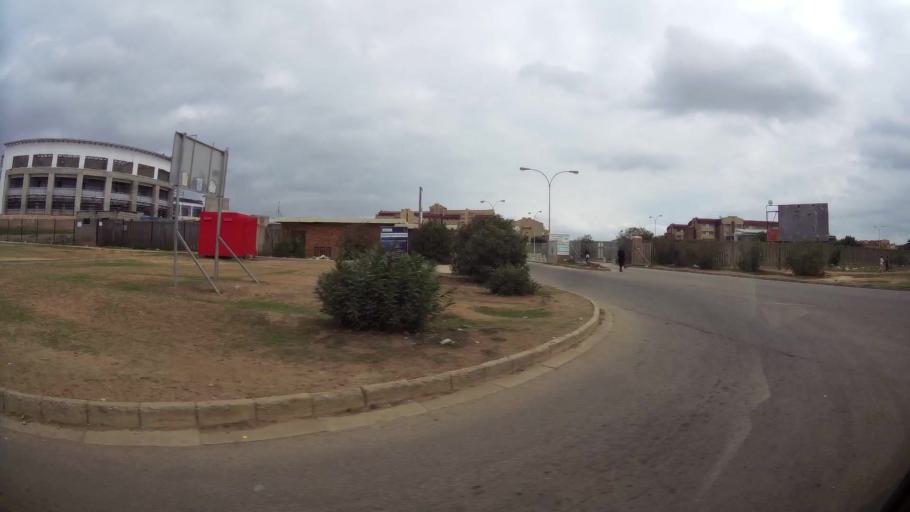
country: ZA
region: Eastern Cape
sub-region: Nelson Mandela Bay Metropolitan Municipality
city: Port Elizabeth
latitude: -33.8787
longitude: 25.5631
